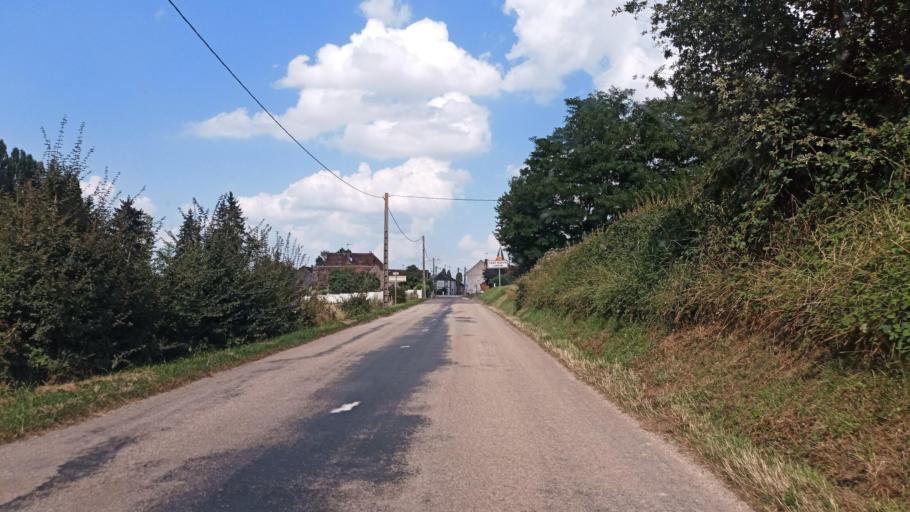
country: FR
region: Bourgogne
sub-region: Departement de l'Yonne
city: Egriselles-le-Bocage
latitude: 48.0212
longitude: 3.1723
